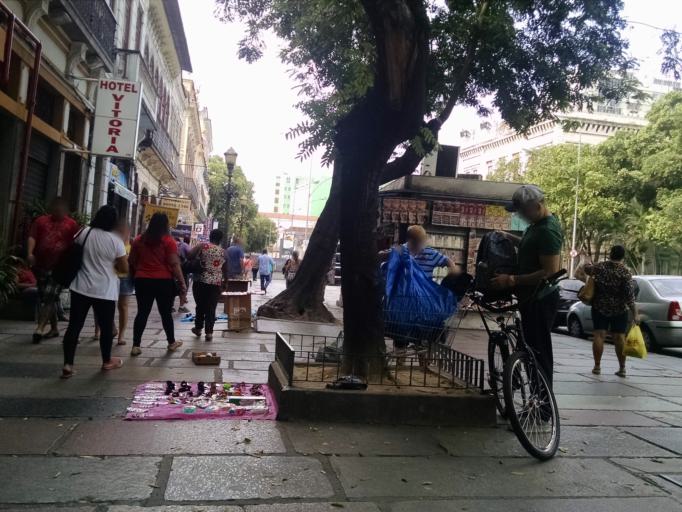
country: BR
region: Rio de Janeiro
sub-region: Rio De Janeiro
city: Rio de Janeiro
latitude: -22.9267
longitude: -43.1766
